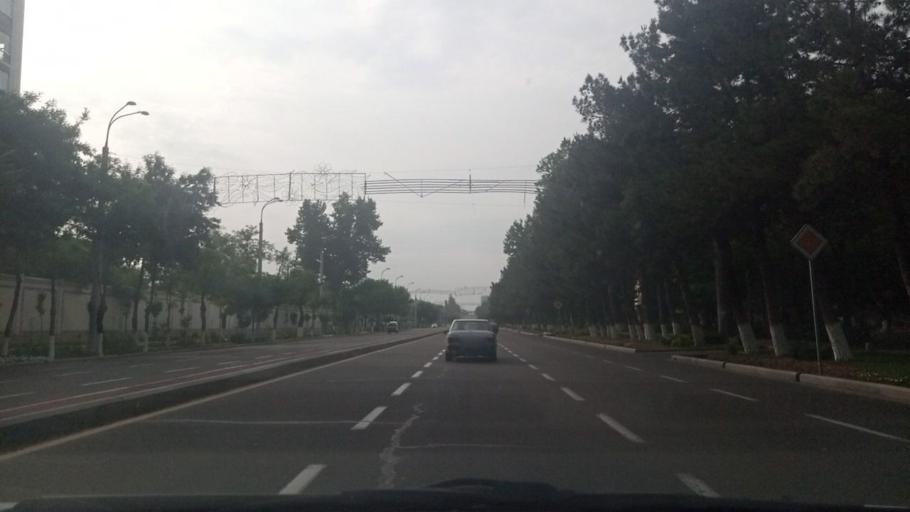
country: UZ
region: Toshkent
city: Salor
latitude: 41.3245
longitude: 69.3624
